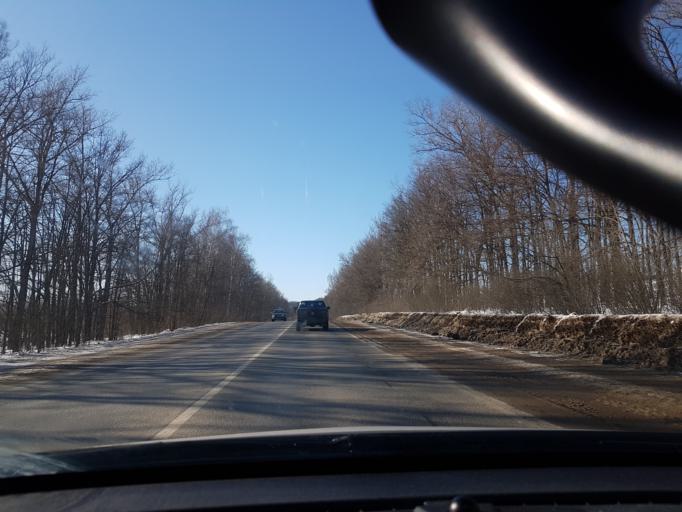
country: RU
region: Moskovskaya
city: Kostrovo
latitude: 55.9099
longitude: 36.7787
